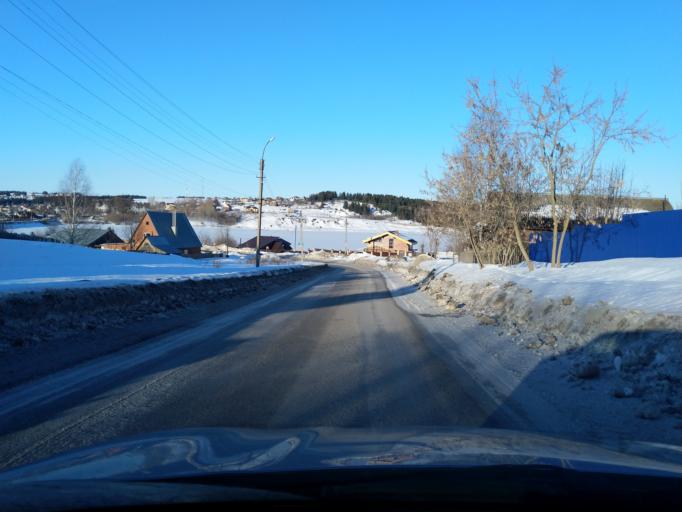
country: RU
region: Perm
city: Polazna
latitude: 58.2989
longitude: 56.4186
